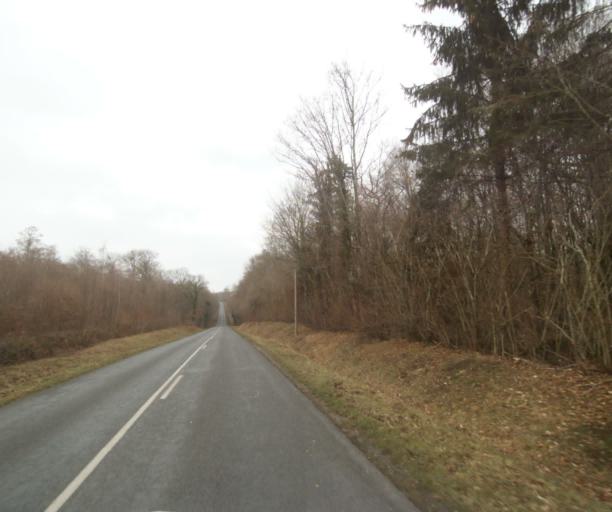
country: FR
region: Champagne-Ardenne
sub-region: Departement de la Haute-Marne
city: Villiers-en-Lieu
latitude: 48.7013
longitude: 4.8948
